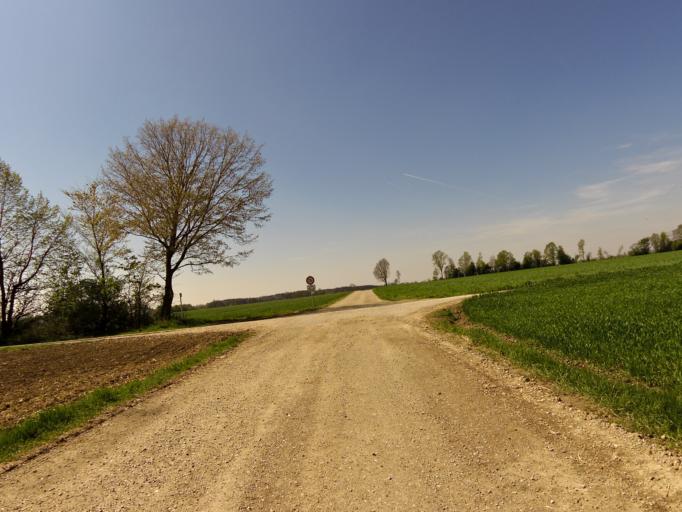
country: DE
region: Bavaria
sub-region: Upper Bavaria
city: Walpertskirchen
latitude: 48.2675
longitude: 11.9610
